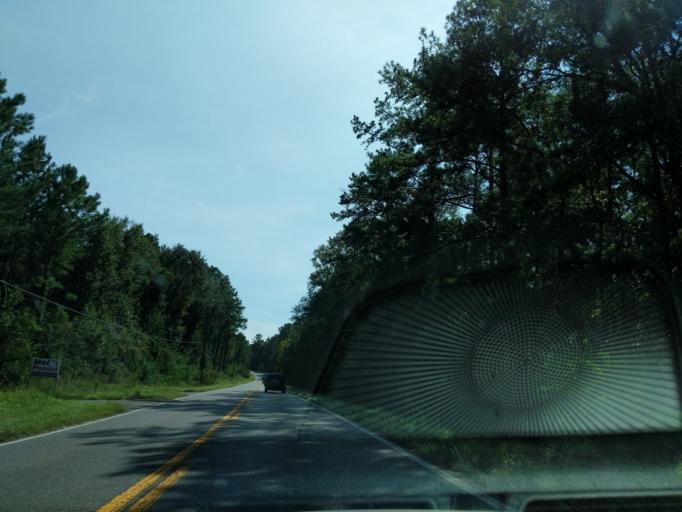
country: US
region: Florida
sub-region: Okaloosa County
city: Crestview
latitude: 30.7403
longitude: -86.6232
